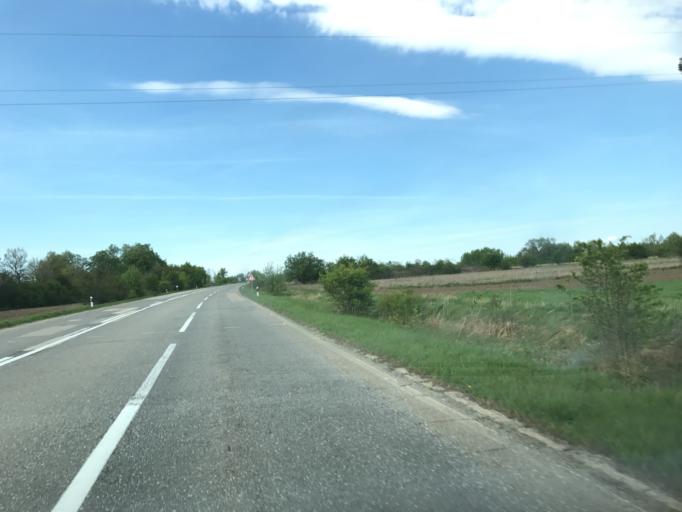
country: RS
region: Central Serbia
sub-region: Borski Okrug
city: Negotin
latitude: 44.1202
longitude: 22.3404
